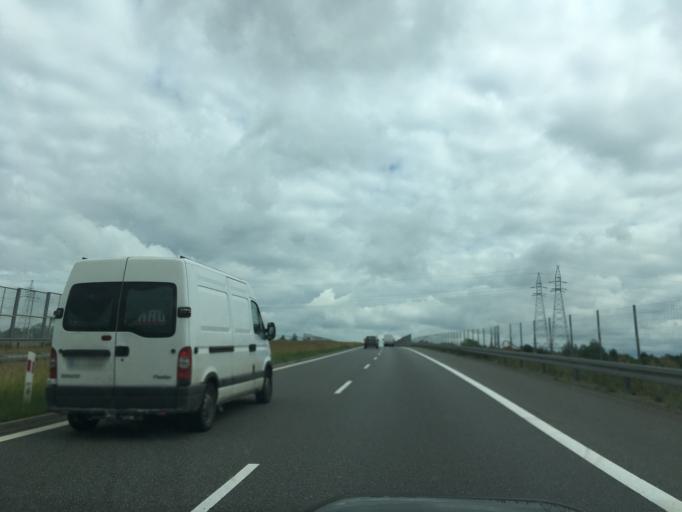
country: PL
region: Lublin Voivodeship
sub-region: Powiat lubelski
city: Jakubowice Murowane
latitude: 51.2881
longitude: 22.6184
